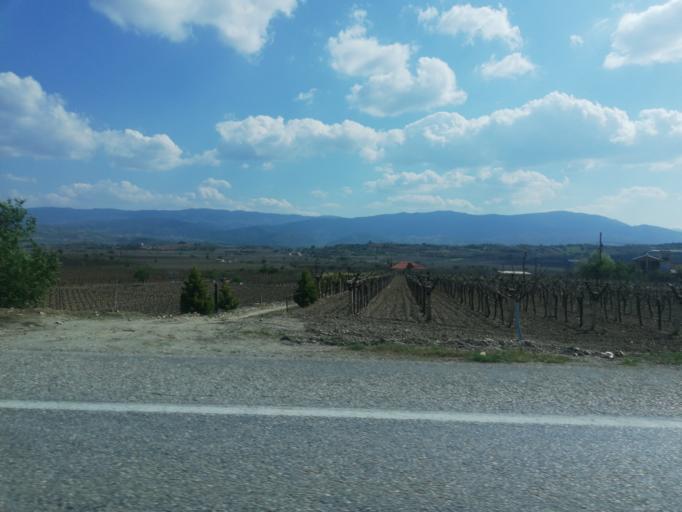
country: TR
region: Manisa
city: Sarigol
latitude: 38.1848
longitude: 28.6762
